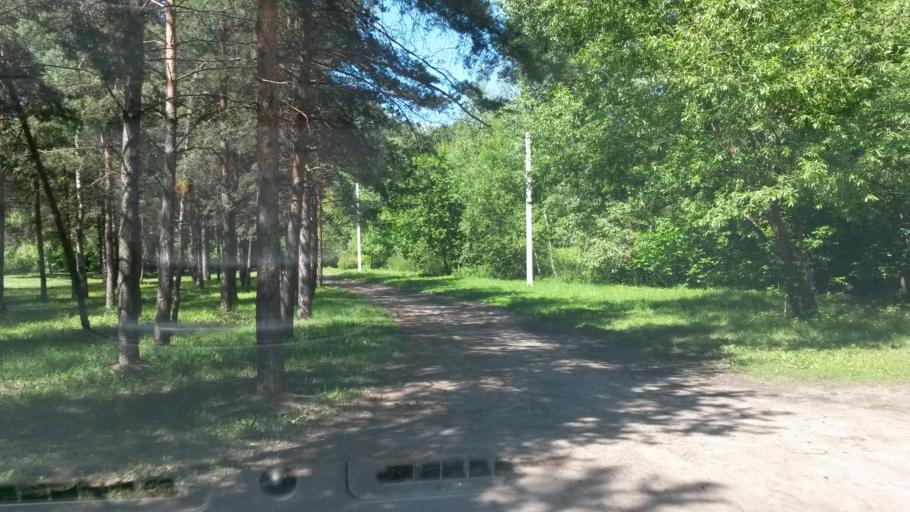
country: RU
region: Jaroslavl
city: Yaroslavl
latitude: 57.6211
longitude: 39.8958
